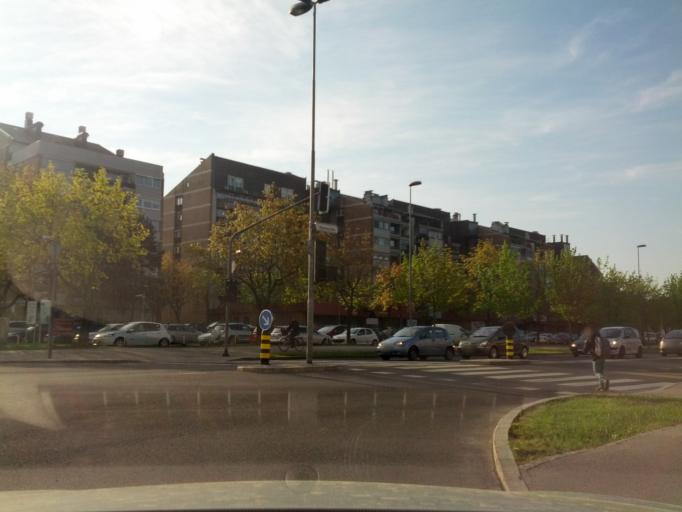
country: SI
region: Ljubljana
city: Ljubljana
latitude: 46.0410
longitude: 14.4995
